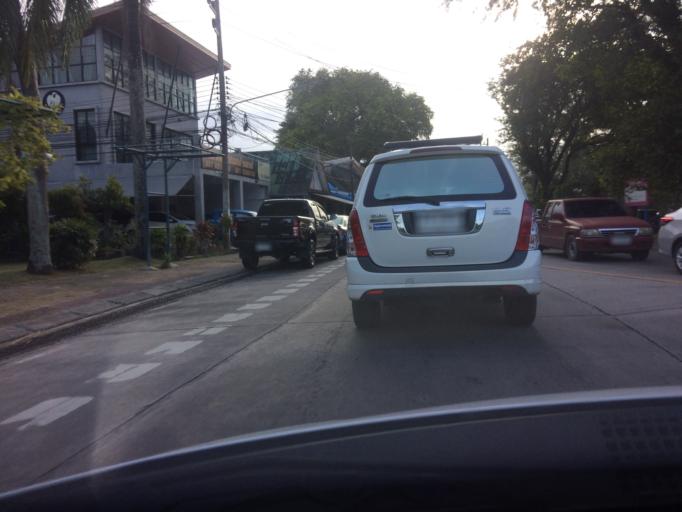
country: TH
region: Phuket
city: Ban Talat Yai
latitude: 7.8699
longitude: 98.3945
